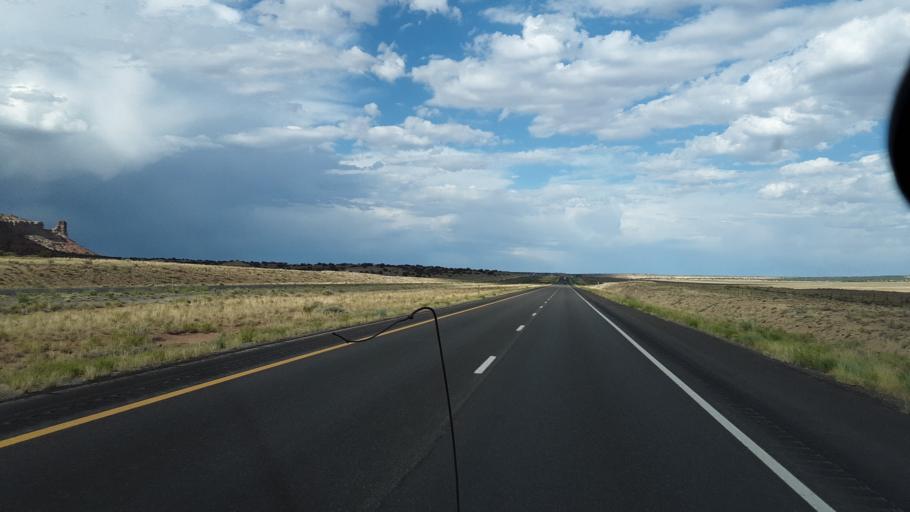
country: US
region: Utah
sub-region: Emery County
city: Castle Dale
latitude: 38.8708
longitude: -110.6881
